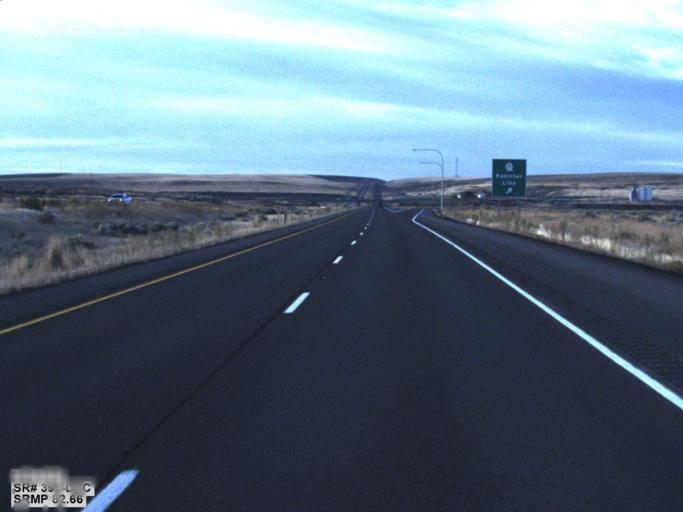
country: US
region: Washington
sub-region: Adams County
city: Ritzville
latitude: 46.9771
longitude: -118.5655
